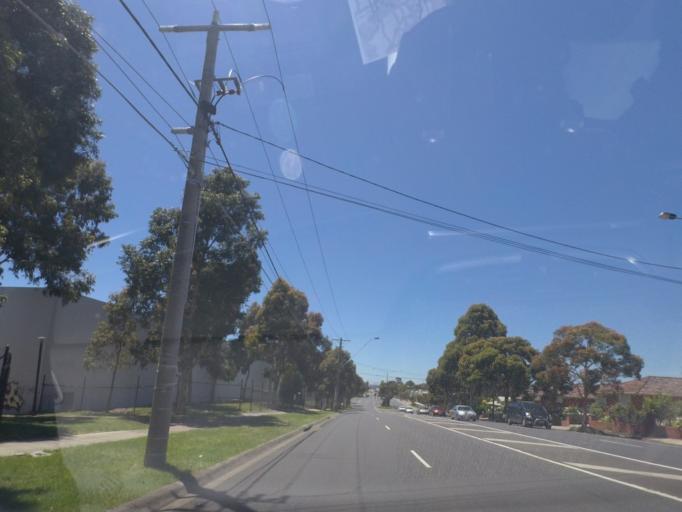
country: AU
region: Victoria
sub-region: Hume
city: Campbellfield
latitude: -37.6886
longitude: 144.9496
